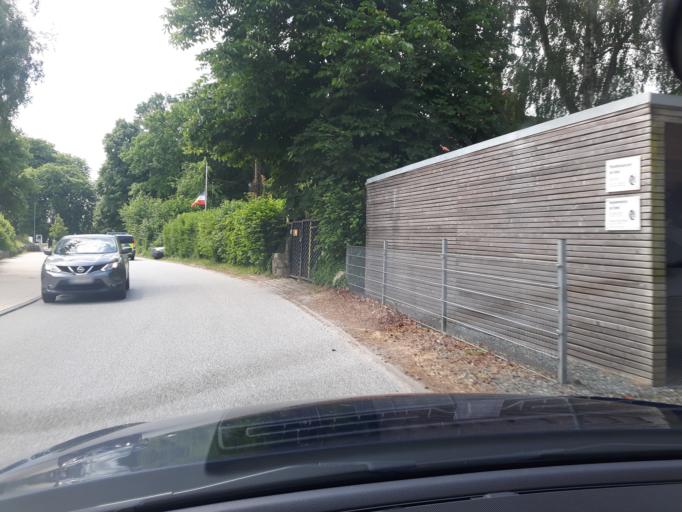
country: DE
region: Schleswig-Holstein
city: Sierksdorf
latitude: 54.0677
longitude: 10.7695
